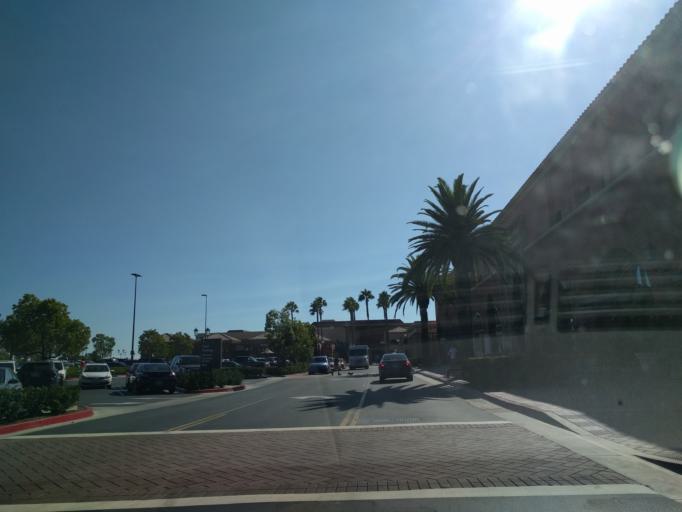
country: US
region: California
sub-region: Orange County
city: San Joaquin Hills
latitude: 33.6161
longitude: -117.8739
